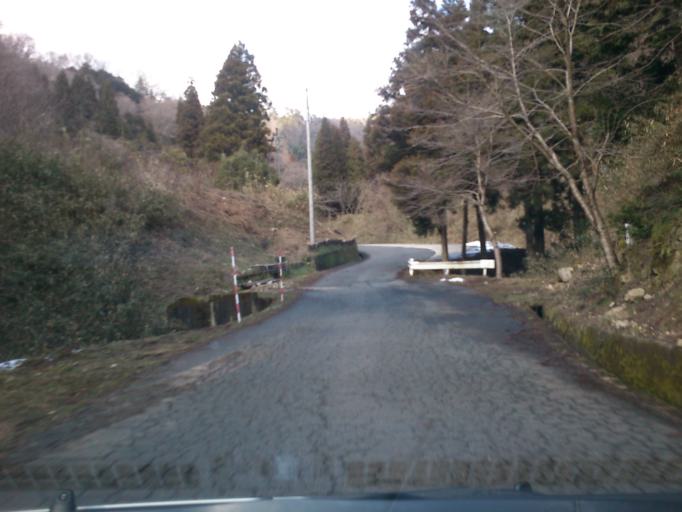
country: JP
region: Kyoto
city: Miyazu
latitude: 35.5886
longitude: 135.1779
